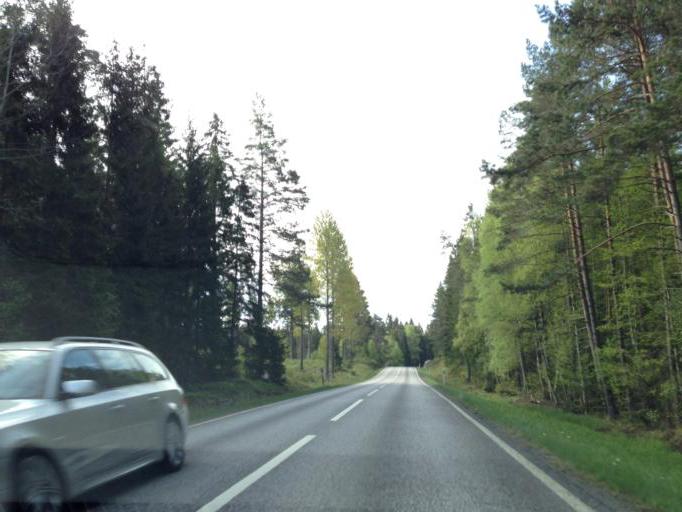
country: SE
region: Soedermanland
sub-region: Nykopings Kommun
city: Stigtomta
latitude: 58.9386
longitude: 16.8459
